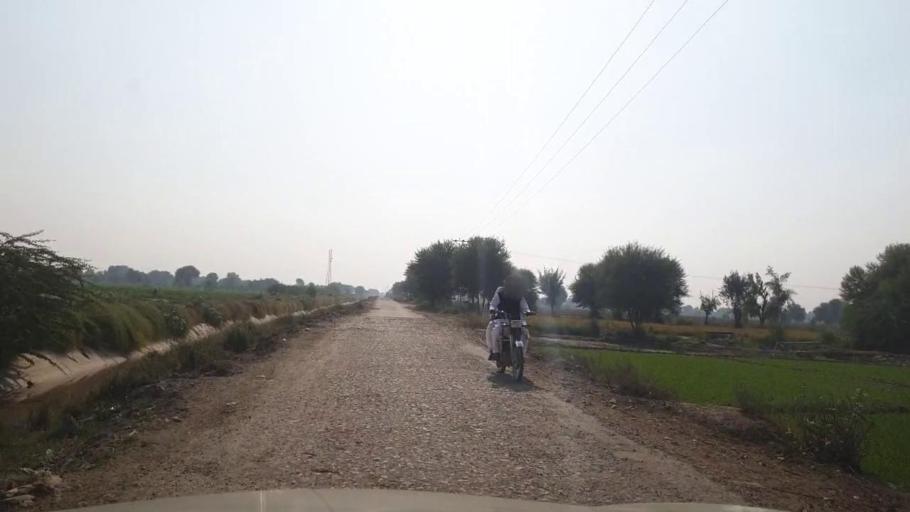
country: PK
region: Sindh
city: Bhan
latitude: 26.5338
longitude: 67.7767
